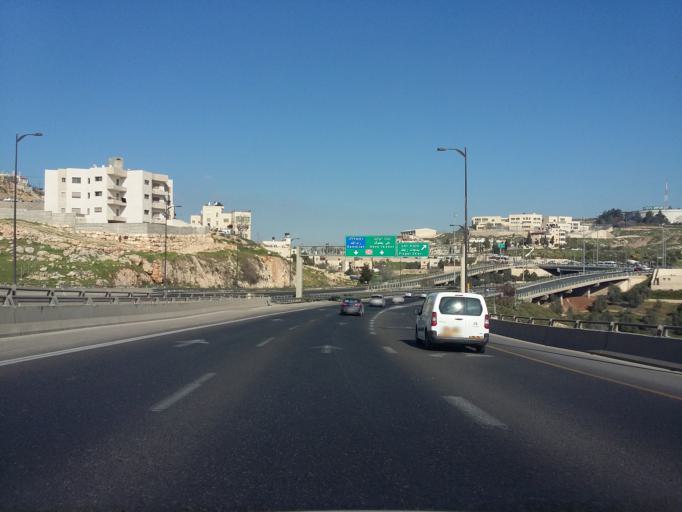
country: PS
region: West Bank
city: `Anata
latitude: 31.8167
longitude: 35.2351
